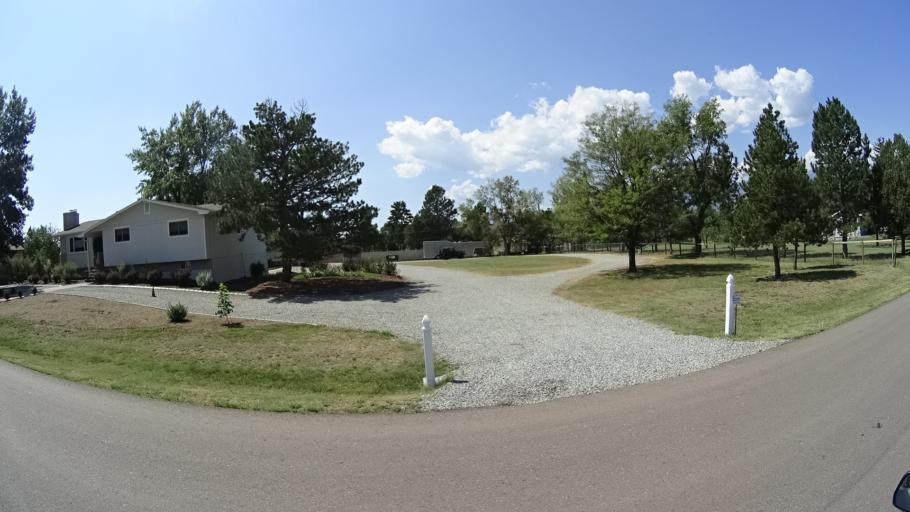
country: US
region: Colorado
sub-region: El Paso County
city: Air Force Academy
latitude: 38.9362
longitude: -104.7863
